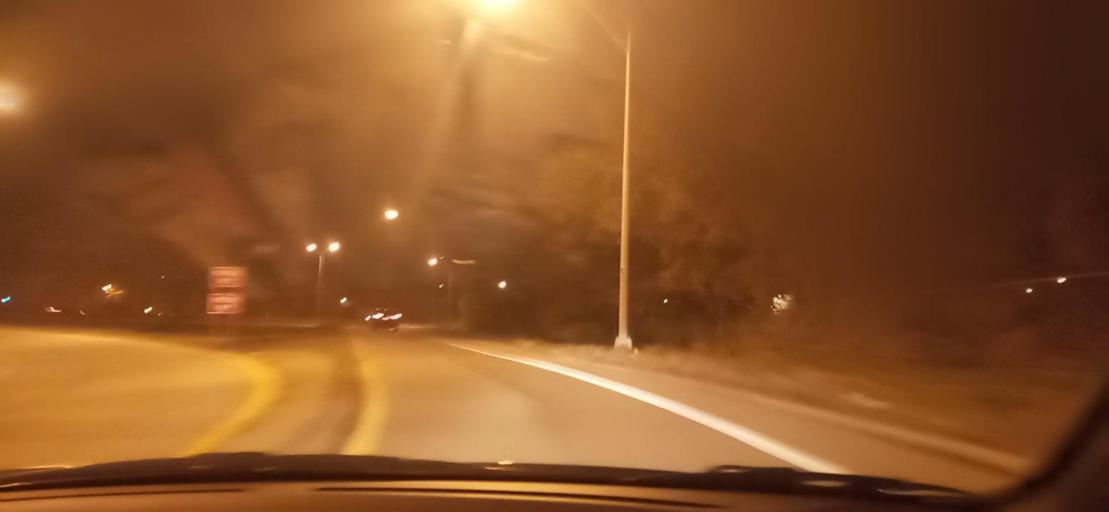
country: US
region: Ohio
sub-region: Summit County
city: Barberton
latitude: 41.0422
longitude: -81.5638
